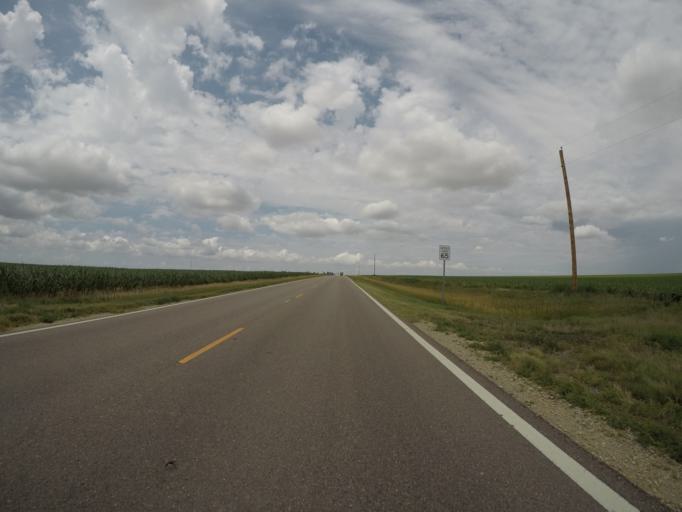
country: US
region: Kansas
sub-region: Rawlins County
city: Atwood
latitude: 39.7148
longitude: -101.0564
